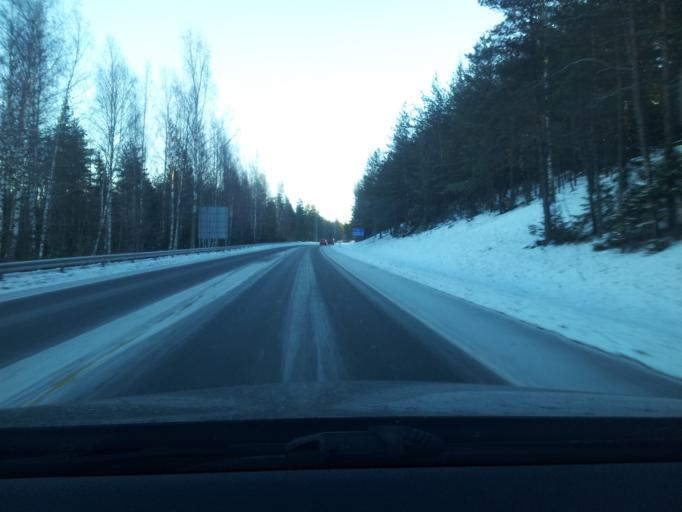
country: FI
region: Uusimaa
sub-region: Helsinki
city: Vihti
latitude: 60.3557
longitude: 24.3368
